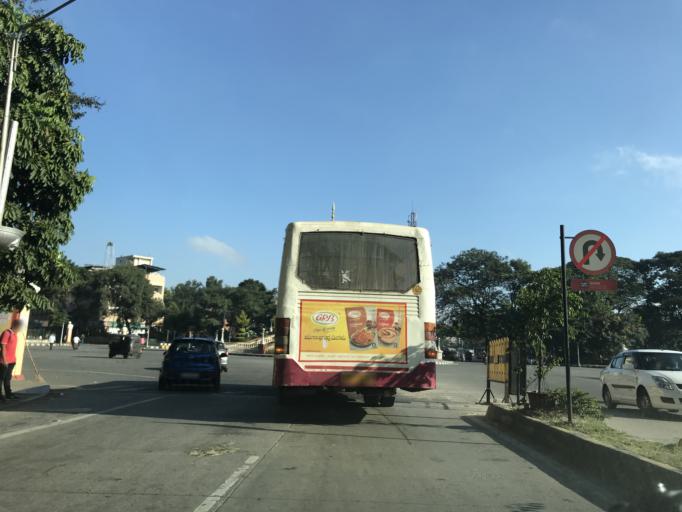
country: IN
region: Karnataka
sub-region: Mysore
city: Mysore
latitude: 12.3066
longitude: 76.6600
